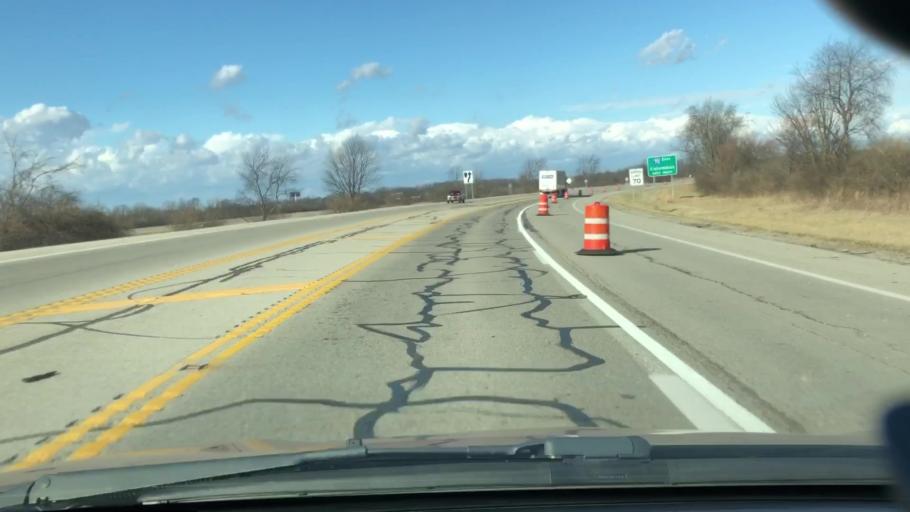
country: US
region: Ohio
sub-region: Clark County
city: Springfield
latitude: 39.8837
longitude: -83.8535
